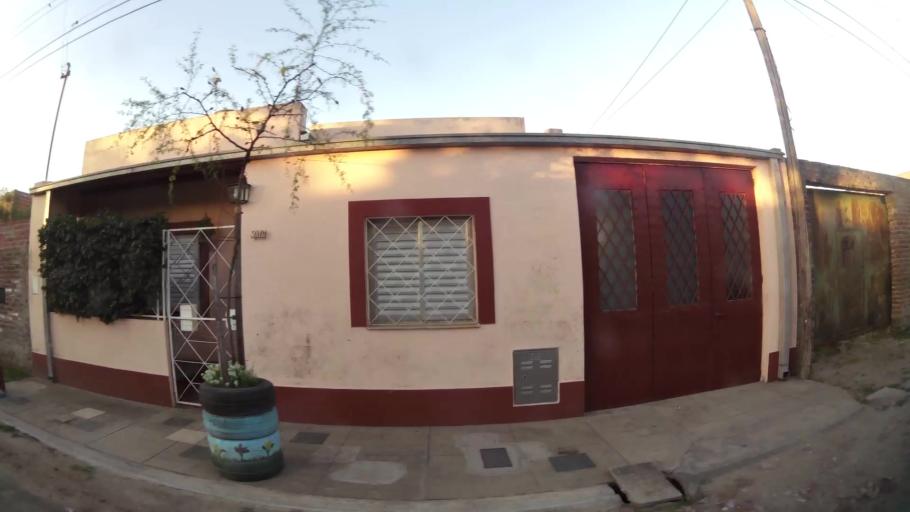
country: AR
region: Santa Fe
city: Santa Fe de la Vera Cruz
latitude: -31.5990
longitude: -60.6992
